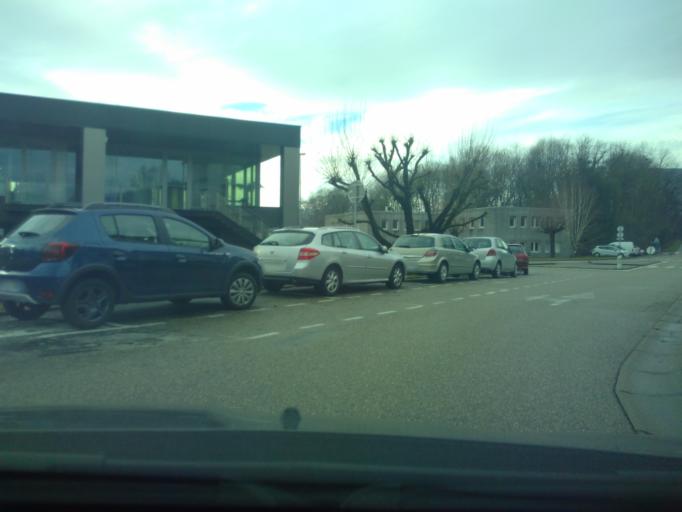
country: FR
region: Rhone-Alpes
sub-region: Departement de l'Isere
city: Montbonnot-Saint-Martin
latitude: 45.2226
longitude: 5.8184
